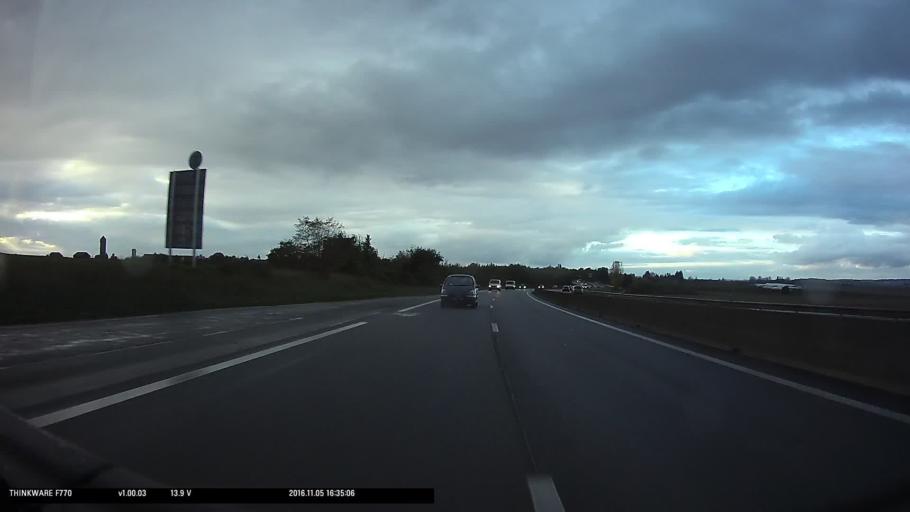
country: FR
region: Ile-de-France
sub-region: Departement du Val-d'Oise
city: Ableiges
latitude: 49.0665
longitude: 1.9741
